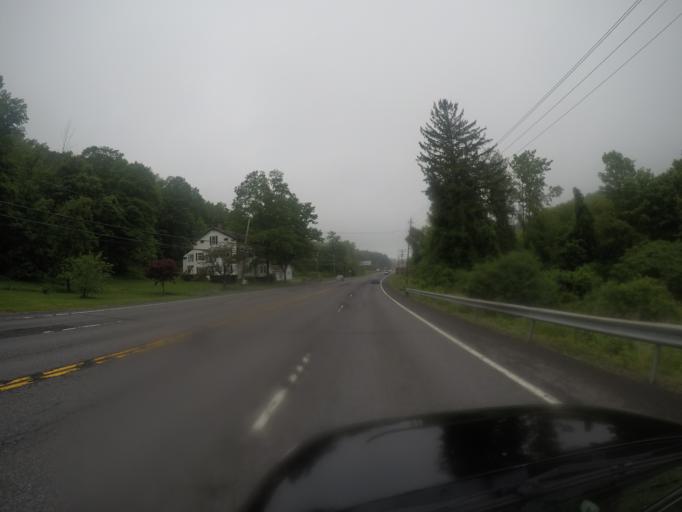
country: US
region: New York
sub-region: Ulster County
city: Hurley
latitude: 41.9588
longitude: -74.0539
